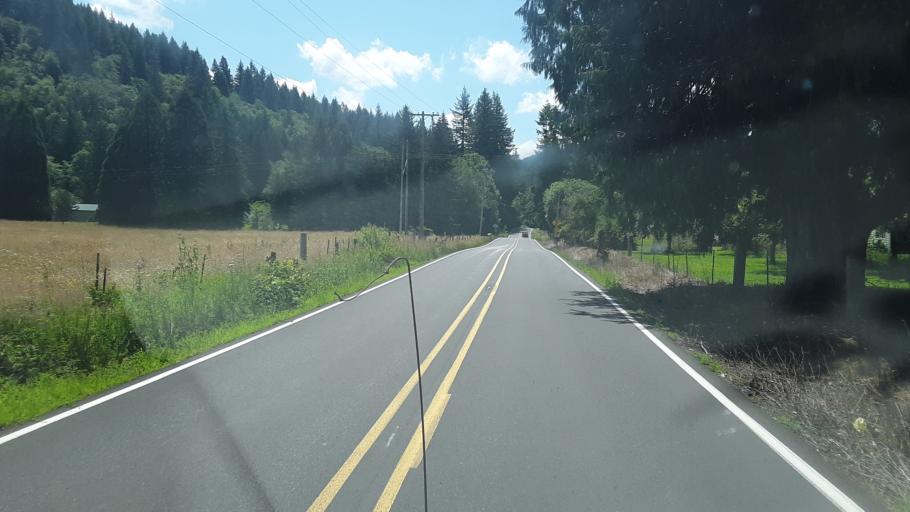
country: US
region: Washington
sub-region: Clark County
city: Amboy
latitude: 45.9400
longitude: -122.3797
